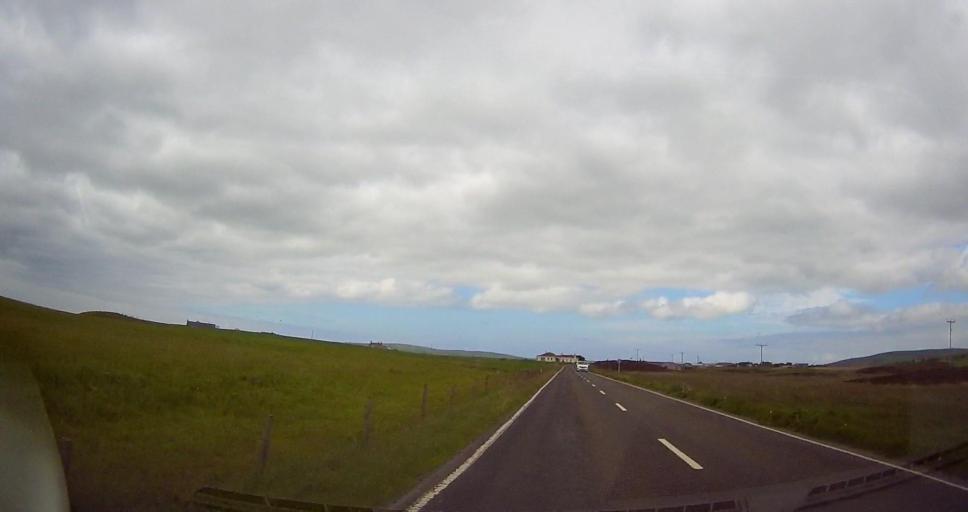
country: GB
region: Scotland
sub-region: Orkney Islands
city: Stromness
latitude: 59.0534
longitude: -3.2108
